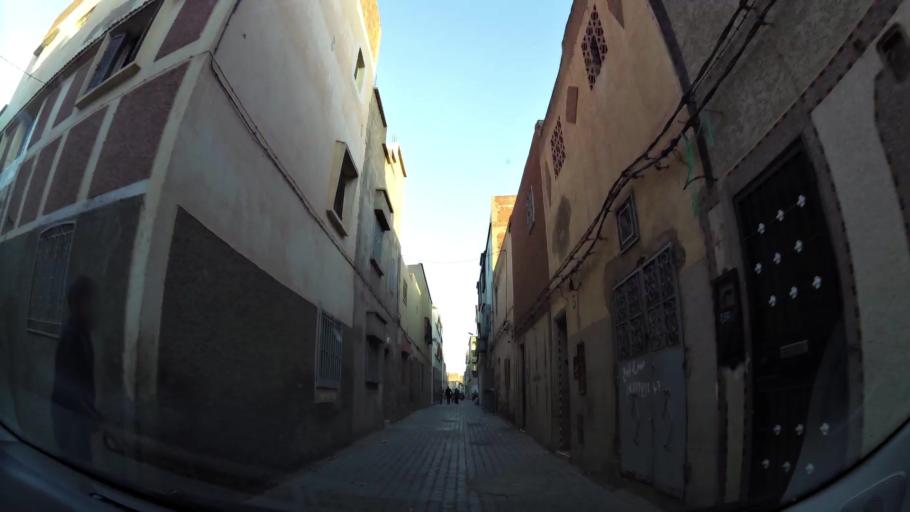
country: MA
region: Oriental
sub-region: Oujda-Angad
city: Oujda
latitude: 34.7022
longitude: -1.9230
